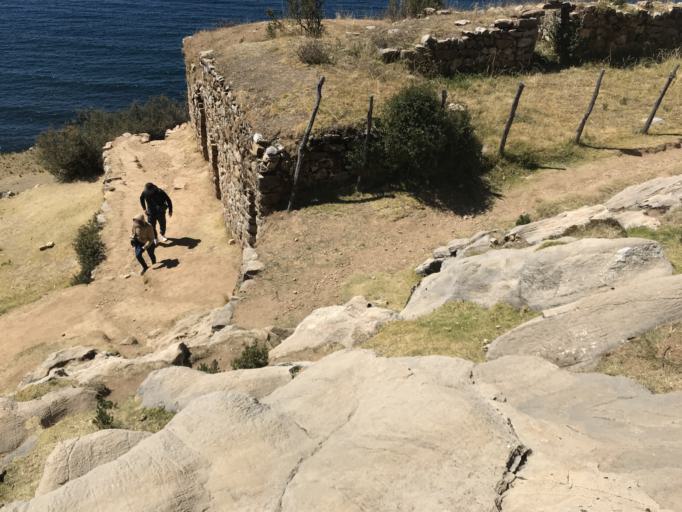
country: BO
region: La Paz
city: Yumani
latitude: -16.0490
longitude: -69.1446
